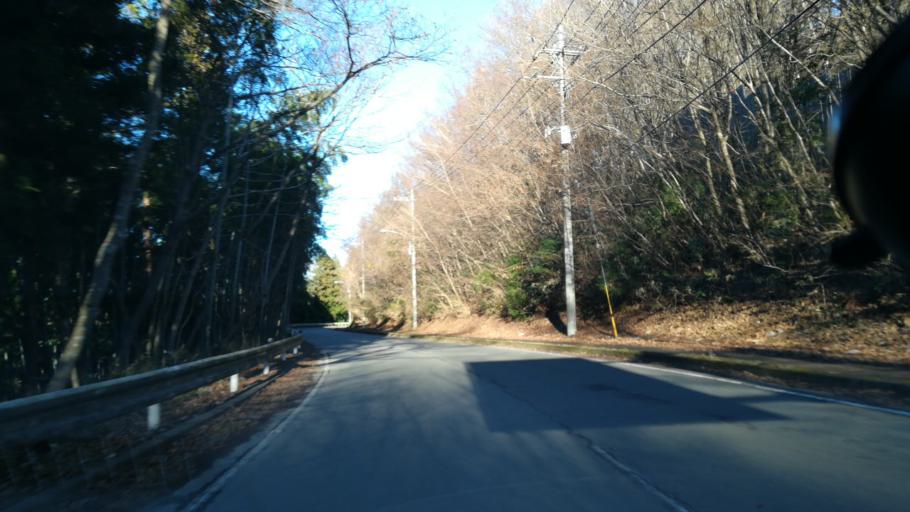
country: JP
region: Tokyo
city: Hachioji
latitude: 35.5524
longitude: 139.2577
